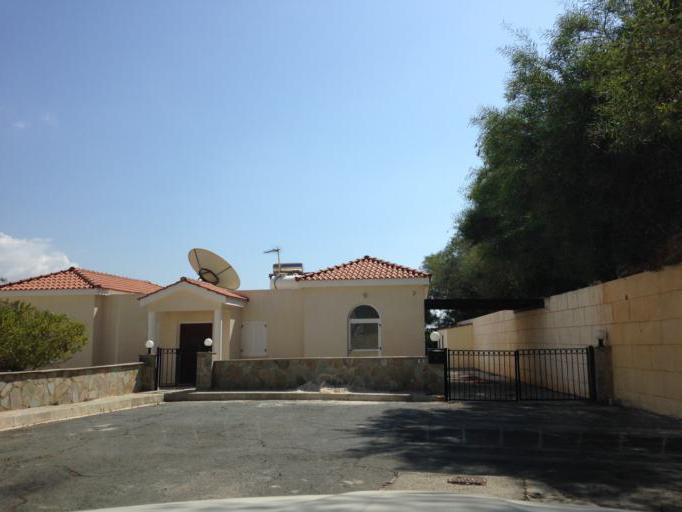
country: CY
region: Pafos
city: Pegeia
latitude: 34.8880
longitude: 32.3854
